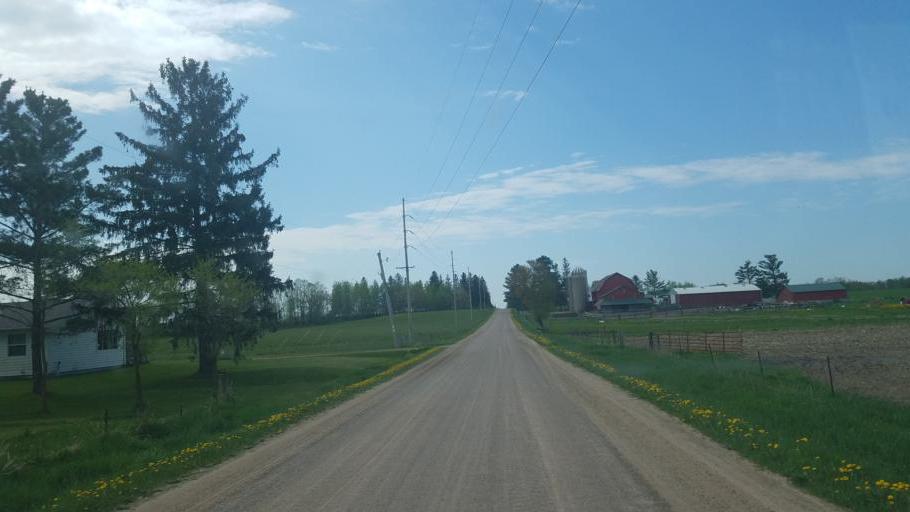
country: US
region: Wisconsin
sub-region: Marathon County
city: Spencer
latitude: 44.6228
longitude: -90.3766
